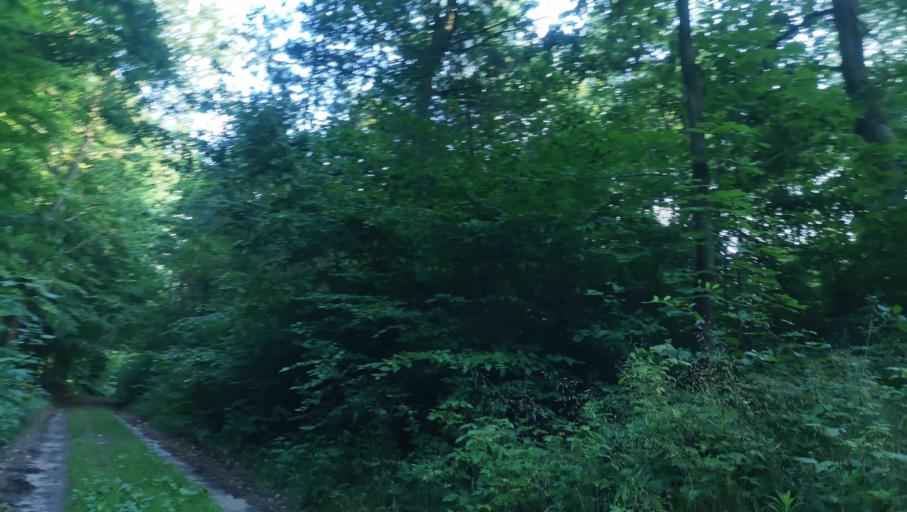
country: PL
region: Greater Poland Voivodeship
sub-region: Powiat jarocinski
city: Witaszyce
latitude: 51.9764
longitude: 17.5474
